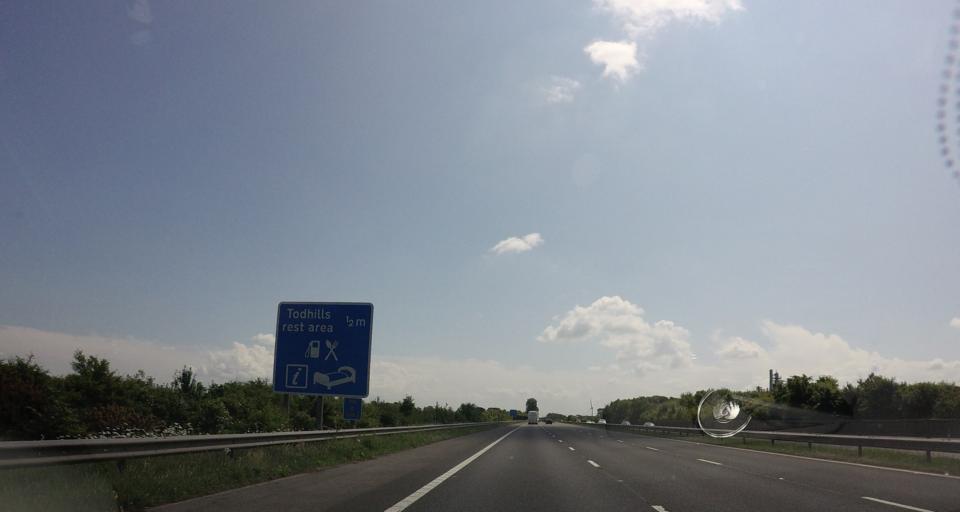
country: GB
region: Scotland
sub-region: Dumfries and Galloway
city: Gretna
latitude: 54.9619
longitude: -2.9927
